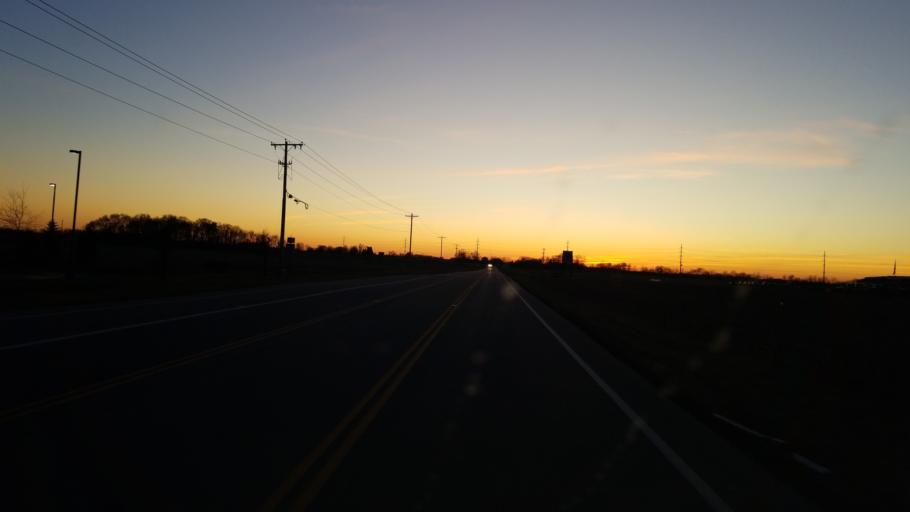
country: US
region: Ohio
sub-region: Fayette County
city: Washington Court House
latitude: 39.5209
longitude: -83.4653
